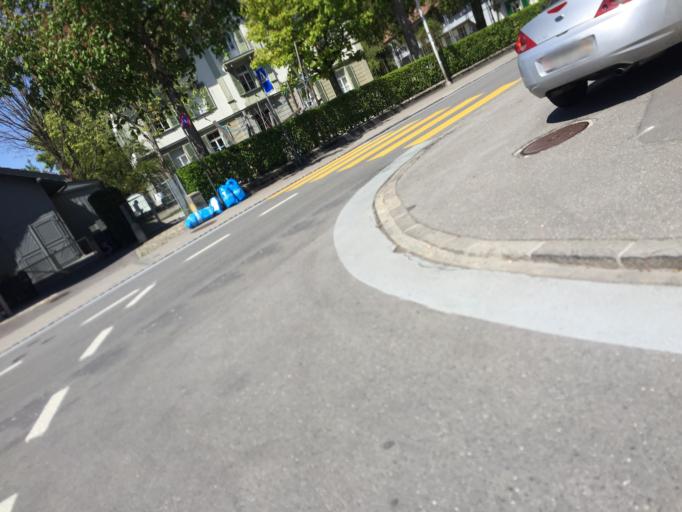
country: CH
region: Bern
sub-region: Bern-Mittelland District
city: Koniz
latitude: 46.9427
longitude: 7.3909
